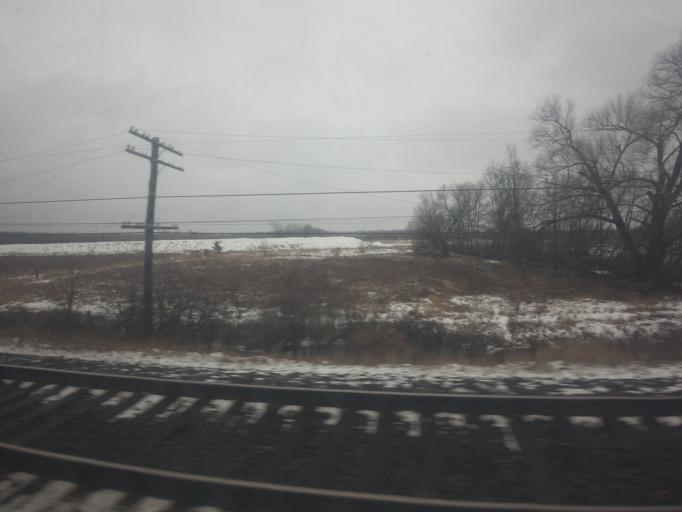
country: CA
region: Ontario
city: Quinte West
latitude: 44.1379
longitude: -77.5316
